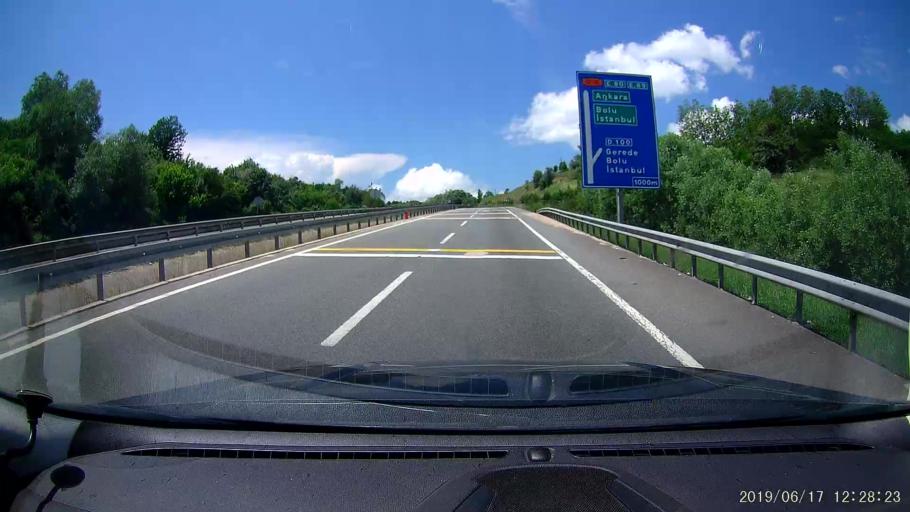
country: TR
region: Bolu
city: Gerede
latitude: 40.8091
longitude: 32.2515
